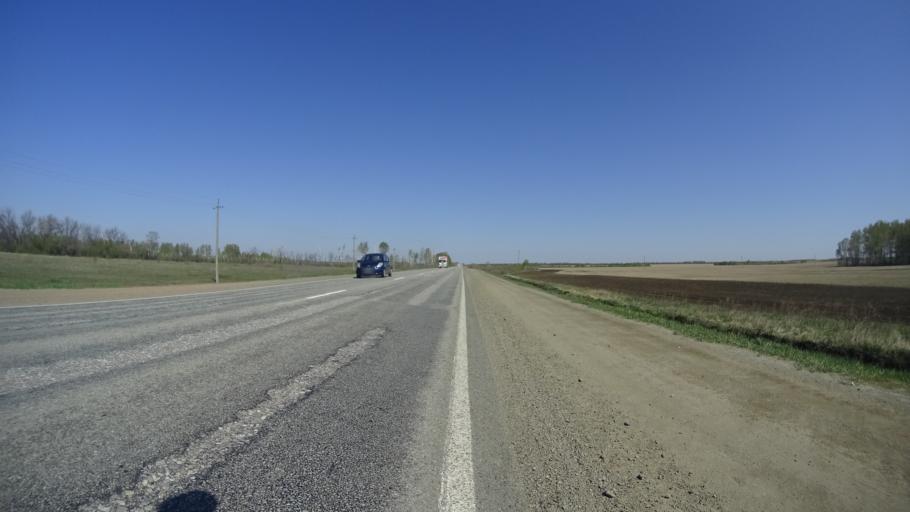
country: RU
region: Chelyabinsk
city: Troitsk
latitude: 54.1930
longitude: 61.4332
